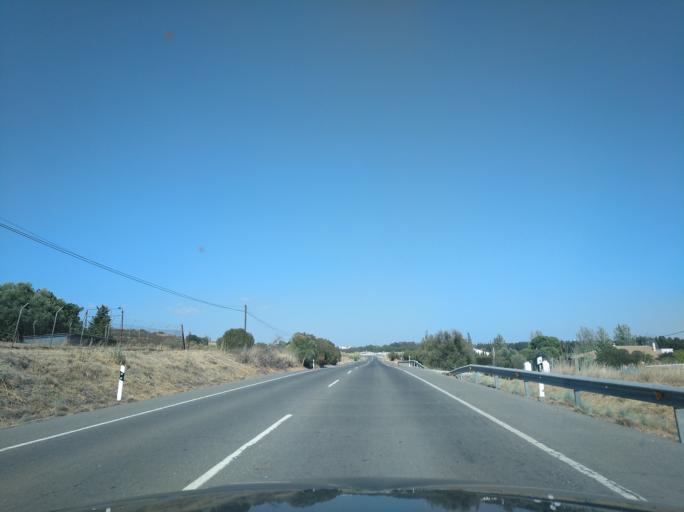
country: ES
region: Andalusia
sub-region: Provincia de Huelva
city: Gibraleon
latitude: 37.3594
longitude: -6.9913
